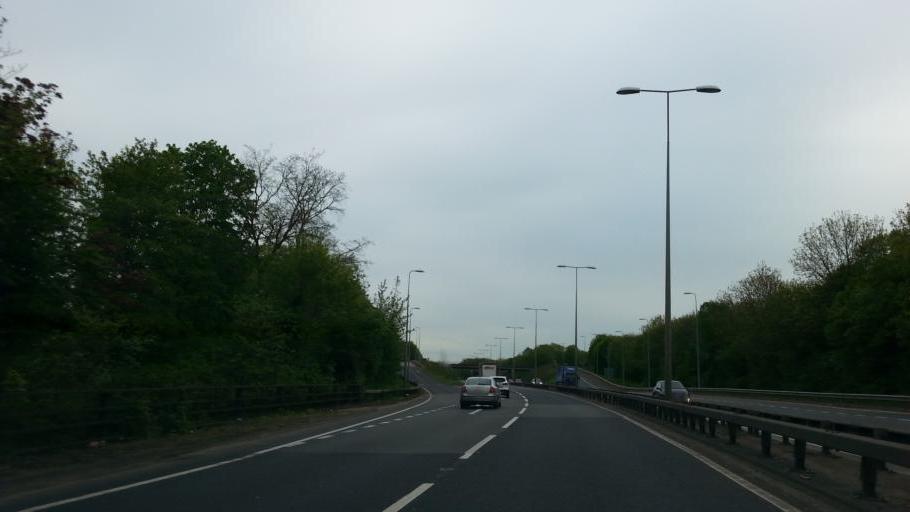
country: GB
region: England
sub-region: Peterborough
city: Marholm
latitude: 52.5912
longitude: -0.2803
